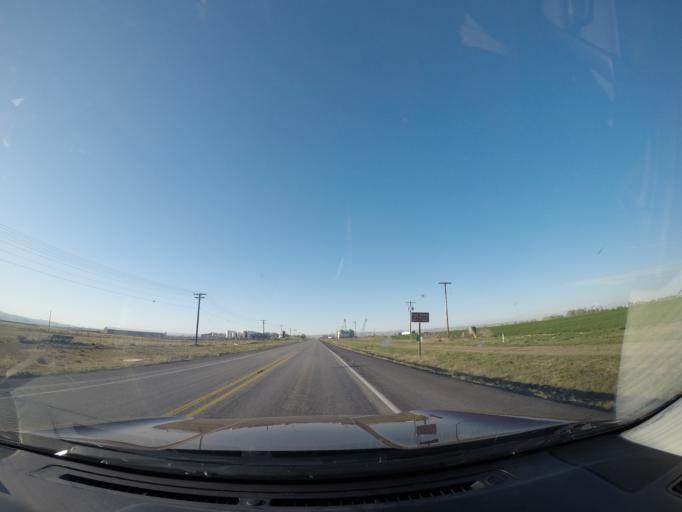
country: US
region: Washington
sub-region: Grant County
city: Quincy
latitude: 47.0954
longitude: -119.8535
